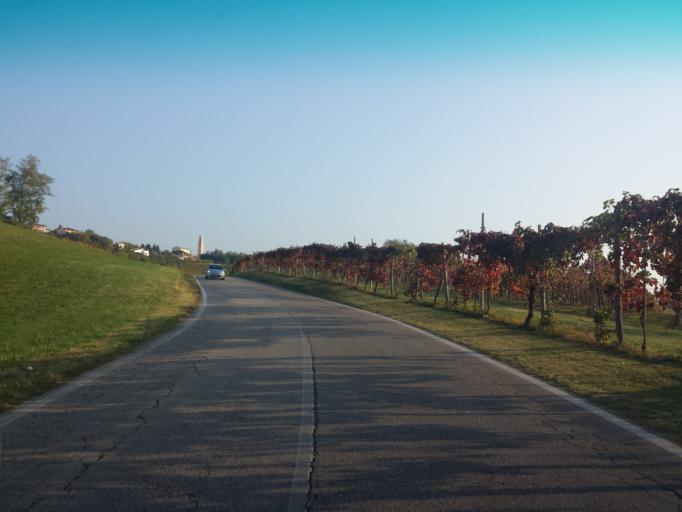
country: IT
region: Veneto
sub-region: Provincia di Vicenza
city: Breganze
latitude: 45.7224
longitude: 11.5797
